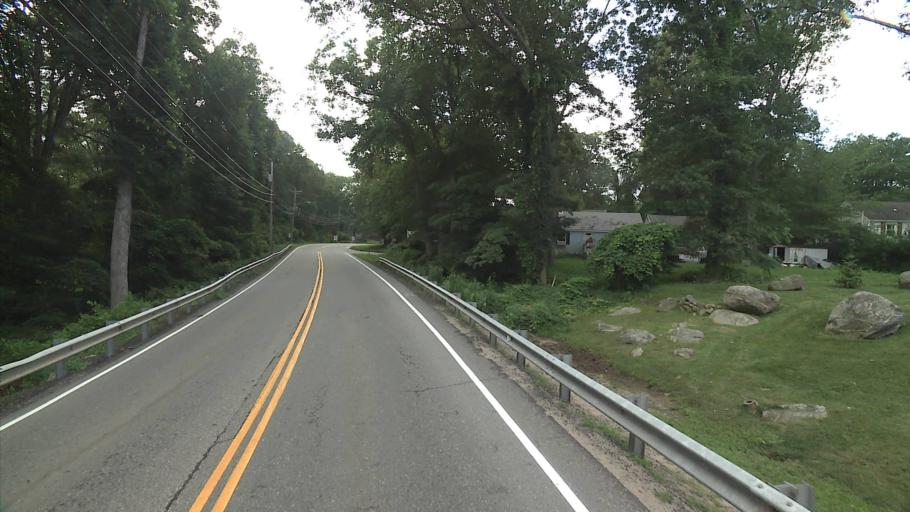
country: US
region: Connecticut
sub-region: Middlesex County
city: Clinton
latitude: 41.3056
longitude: -72.5351
